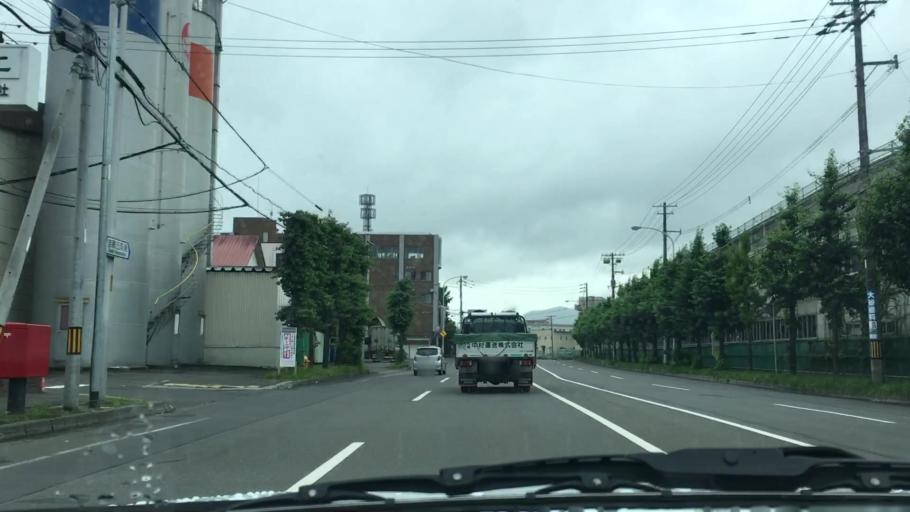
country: JP
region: Hokkaido
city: Sapporo
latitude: 43.0726
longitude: 141.3823
